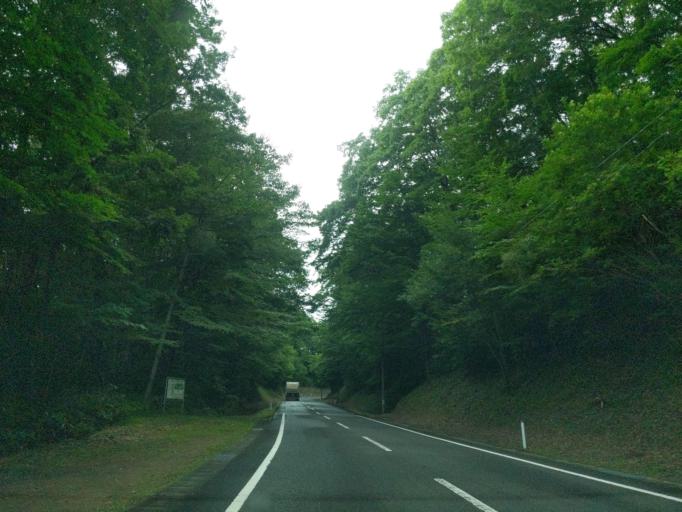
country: JP
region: Tochigi
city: Kuroiso
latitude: 37.2549
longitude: 140.0888
